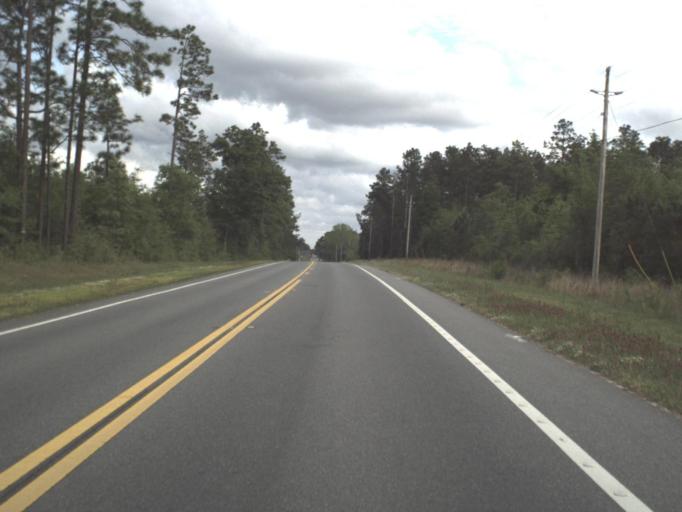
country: US
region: Alabama
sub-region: Escambia County
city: East Brewton
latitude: 30.9569
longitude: -87.0432
